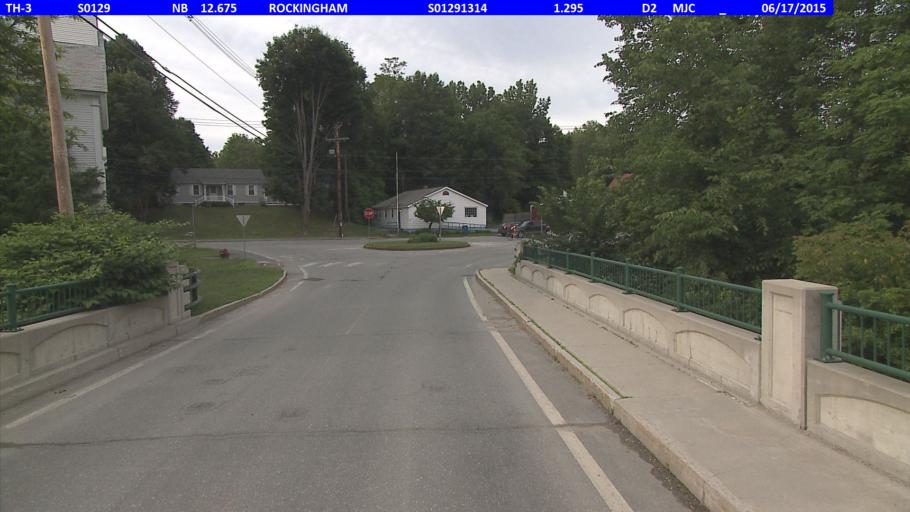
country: US
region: Vermont
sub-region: Windham County
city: Rockingham
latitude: 43.1379
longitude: -72.5097
